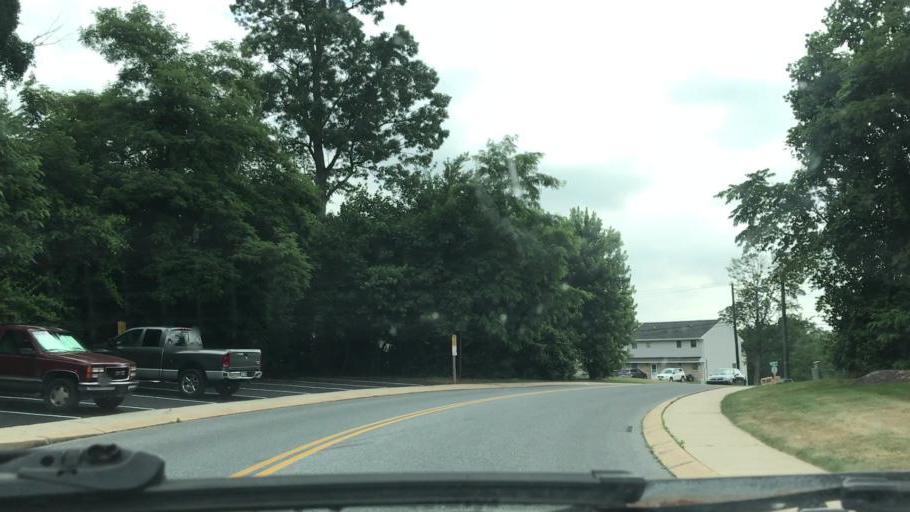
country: US
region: Pennsylvania
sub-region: Lancaster County
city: Elizabethtown
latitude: 40.1685
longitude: -76.6089
